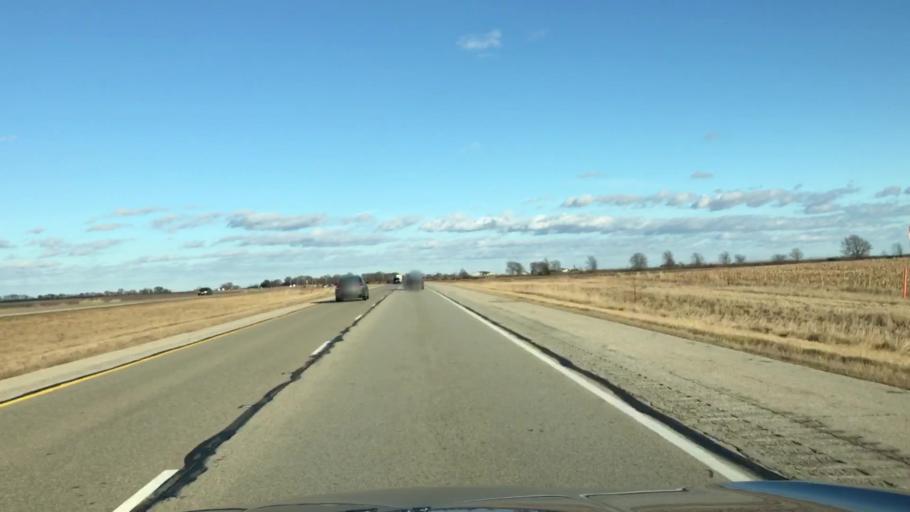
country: US
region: Illinois
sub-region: McLean County
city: Lexington
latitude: 40.5876
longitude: -88.8674
